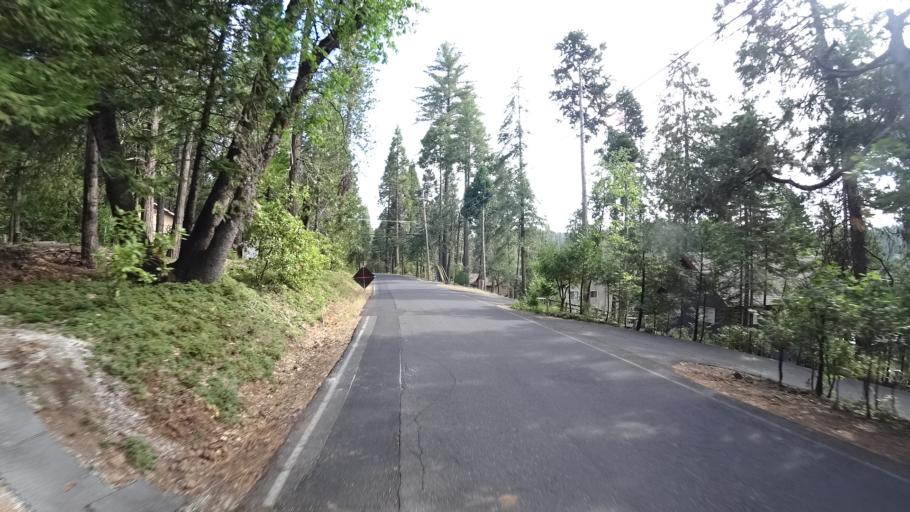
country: US
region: California
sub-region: Calaveras County
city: Arnold
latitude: 38.2612
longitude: -120.3342
